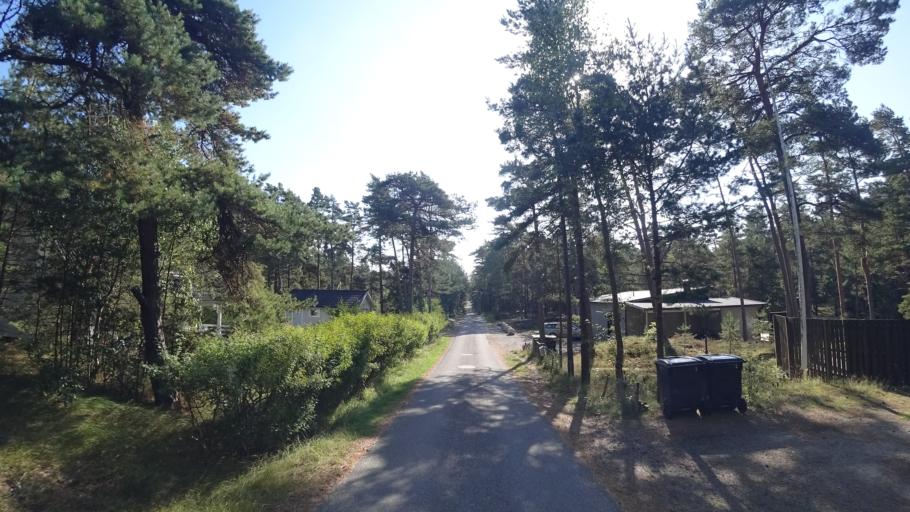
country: SE
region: Skane
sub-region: Kristianstads Kommun
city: Ahus
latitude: 55.9185
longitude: 14.3055
